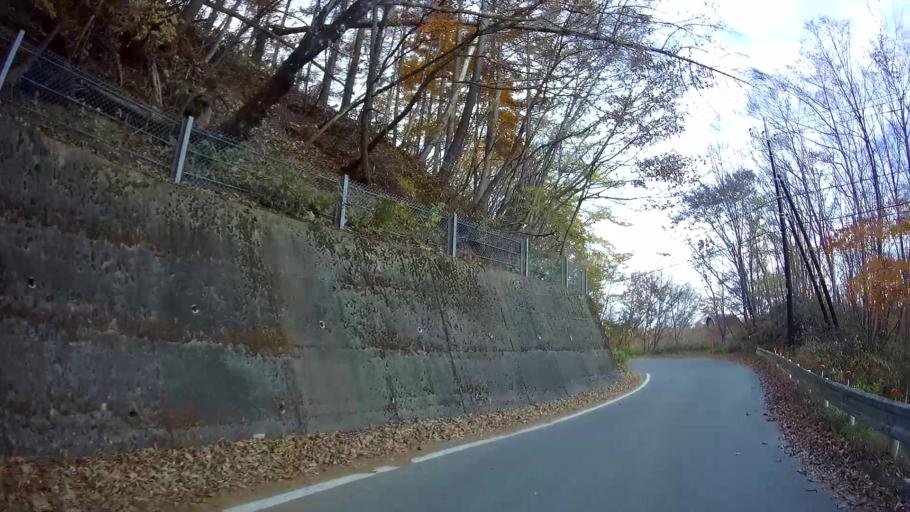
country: JP
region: Gunma
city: Nakanojomachi
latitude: 36.6696
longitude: 138.6708
